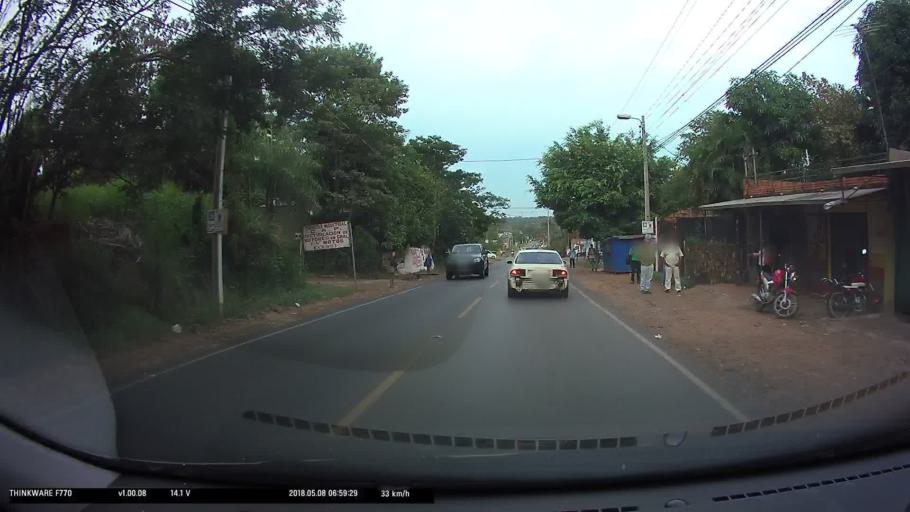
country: PY
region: Central
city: Limpio
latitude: -25.2470
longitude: -57.4843
